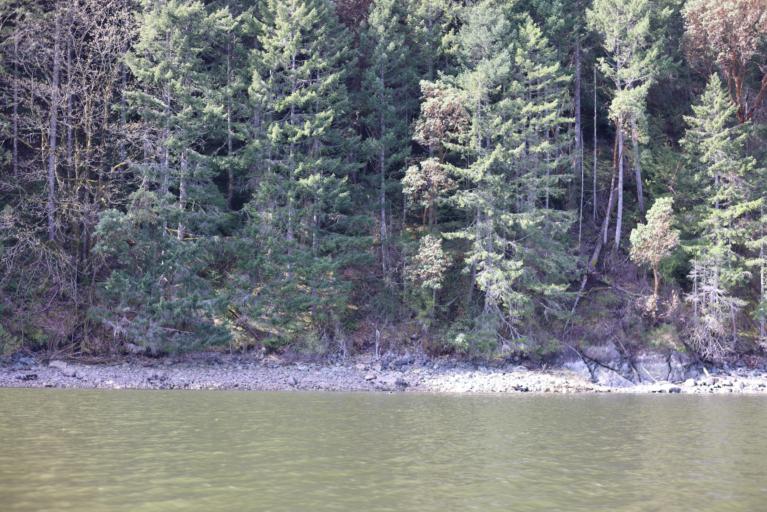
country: CA
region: British Columbia
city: Langford
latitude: 48.5334
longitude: -123.5519
